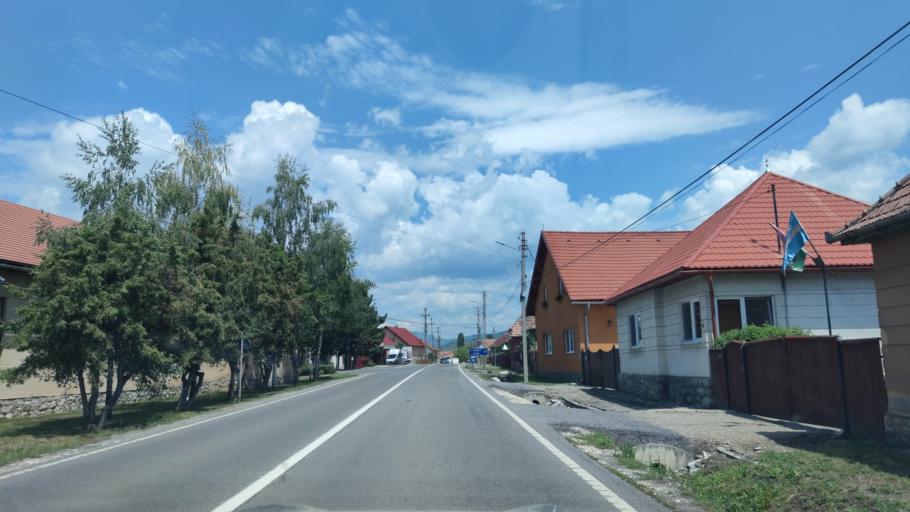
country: RO
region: Harghita
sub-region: Comuna Suseni
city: Valea Stramba
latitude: 46.6915
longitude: 25.5942
